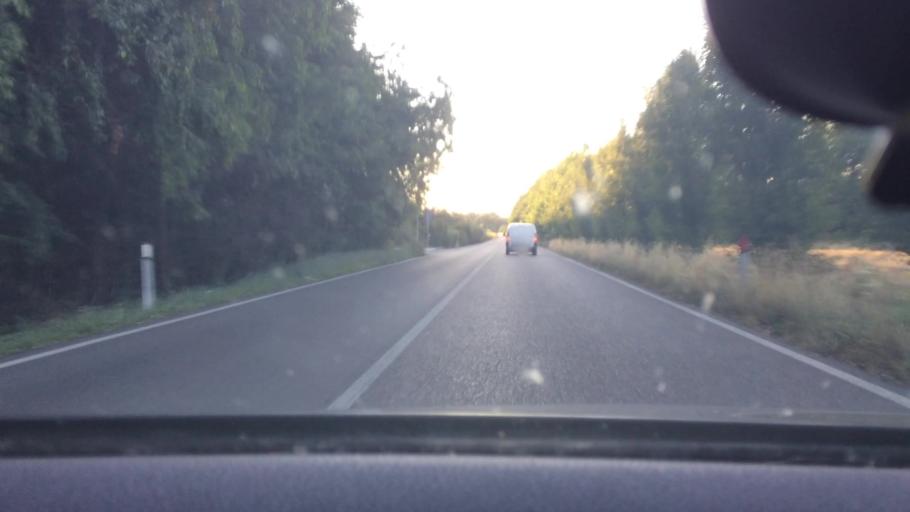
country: IT
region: Lombardy
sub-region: Citta metropolitana di Milano
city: Rescaldina
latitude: 45.6187
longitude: 8.9650
